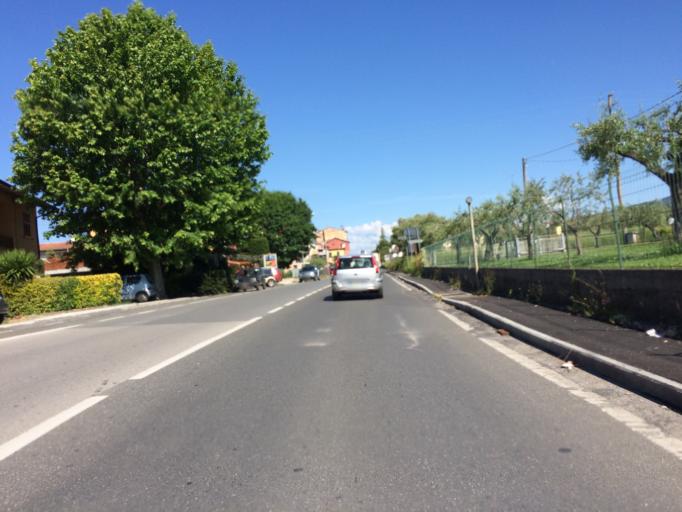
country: IT
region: Tuscany
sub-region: Provincia di Massa-Carrara
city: Borghetto-Melara
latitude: 44.0920
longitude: 9.9941
